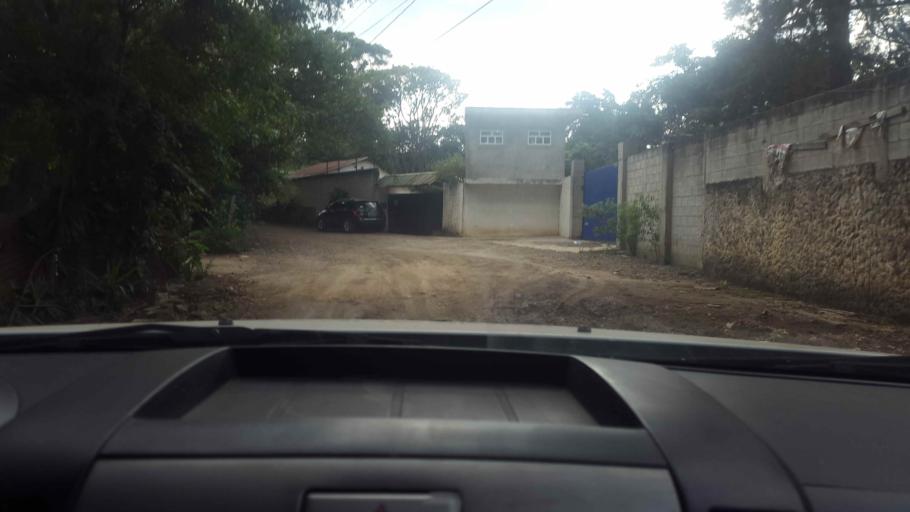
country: GT
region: Guatemala
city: Petapa
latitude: 14.5067
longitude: -90.5391
